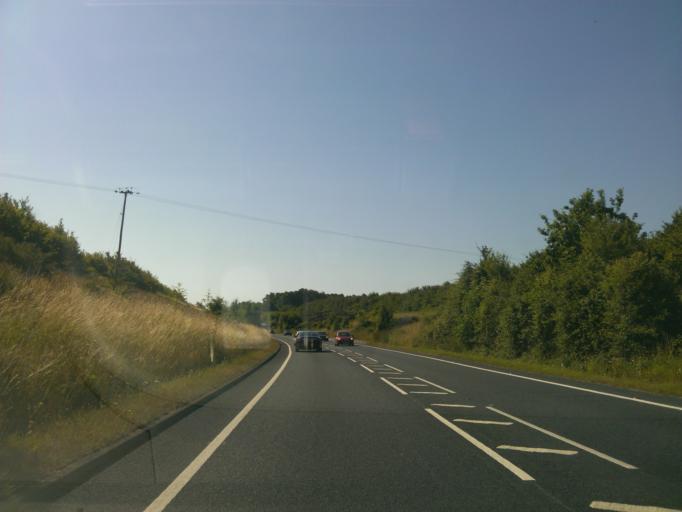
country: GB
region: England
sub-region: Essex
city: Great Bentley
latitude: 51.8481
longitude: 1.1038
